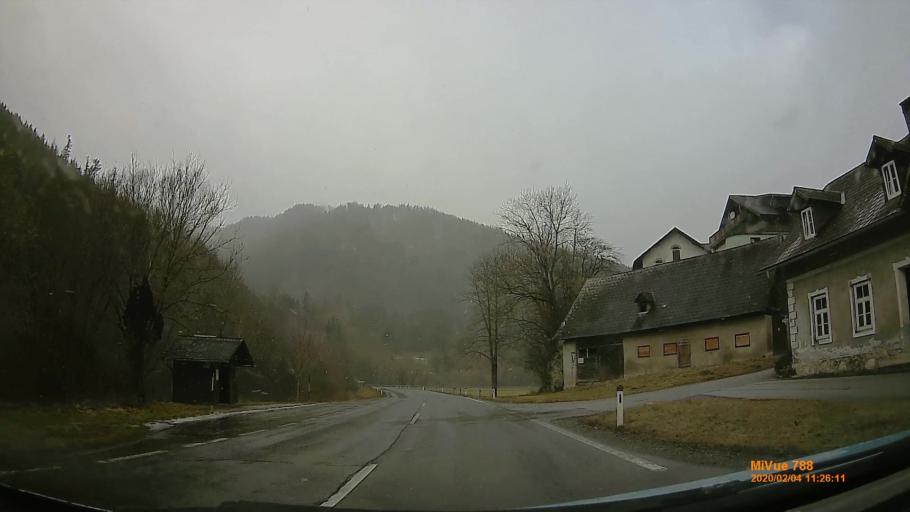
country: AT
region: Styria
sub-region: Politischer Bezirk Bruck-Muerzzuschlag
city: Kapellen
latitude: 47.6382
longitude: 15.6463
